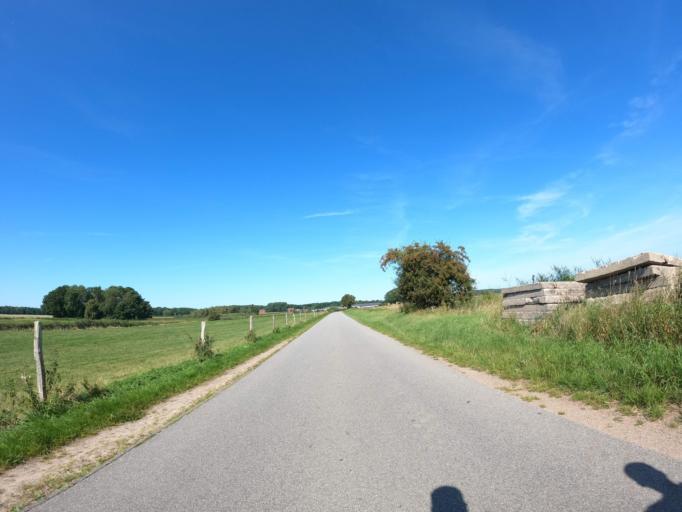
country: DE
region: Mecklenburg-Vorpommern
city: Prohn
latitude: 54.3954
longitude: 13.0231
